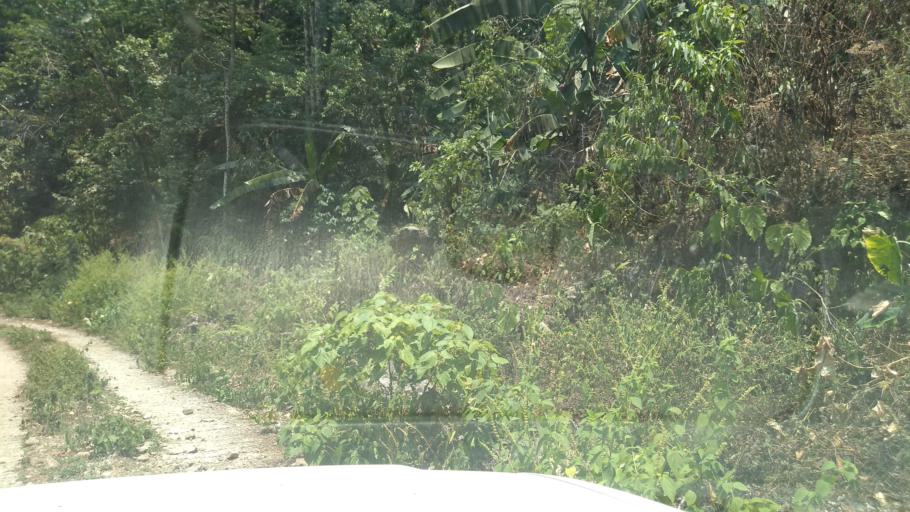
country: MX
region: Veracruz
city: Motzorongo
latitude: 18.6075
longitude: -96.7597
